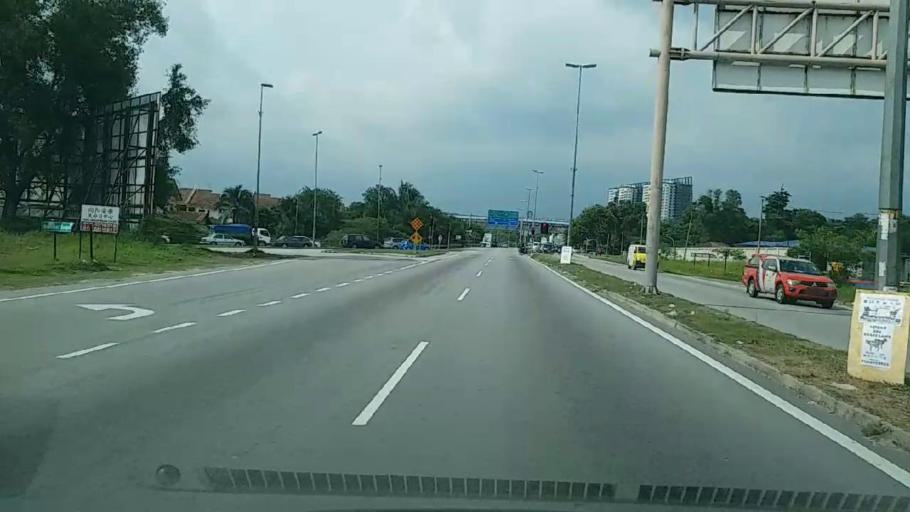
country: MY
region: Selangor
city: Subang Jaya
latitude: 2.9796
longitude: 101.6140
